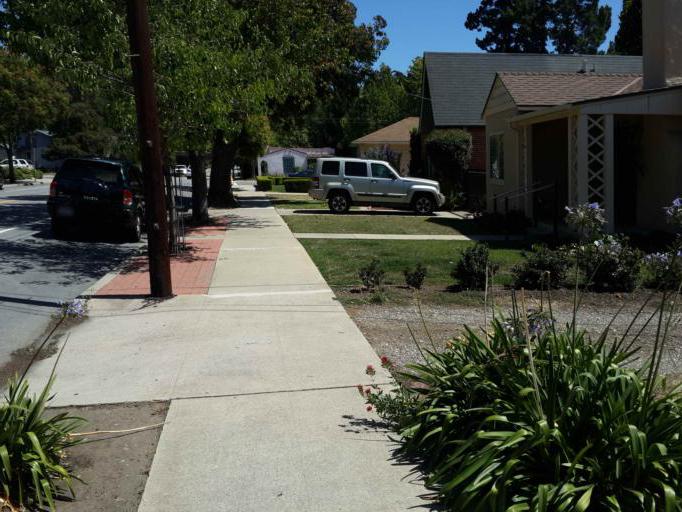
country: US
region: California
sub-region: San Luis Obispo County
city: San Luis Obispo
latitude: 35.2856
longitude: -120.6680
